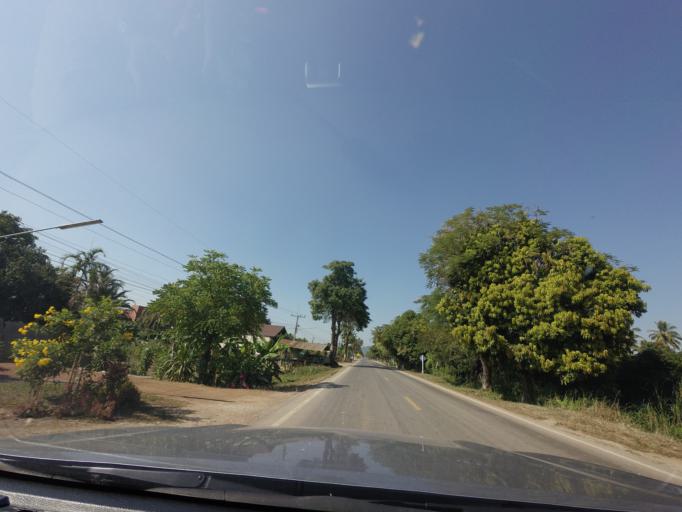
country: TH
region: Sukhothai
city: Sawankhalok
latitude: 17.3683
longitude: 99.8036
